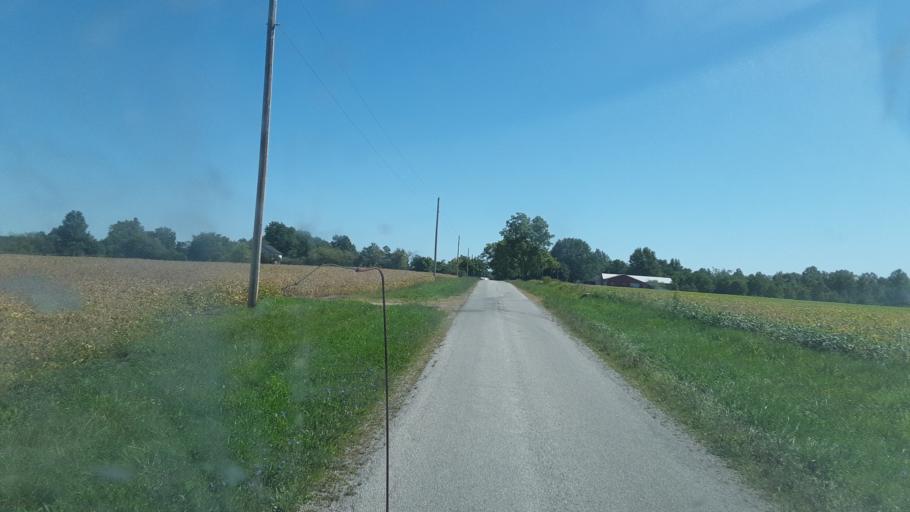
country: US
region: Ohio
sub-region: Sandusky County
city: Mount Carmel
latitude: 41.1467
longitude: -82.9500
